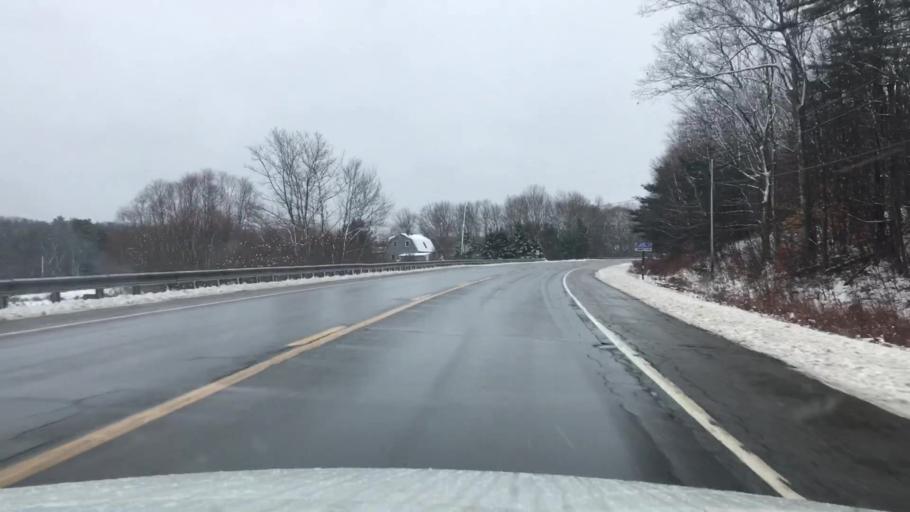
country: US
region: Maine
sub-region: Knox County
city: Rockport
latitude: 44.1734
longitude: -69.1519
